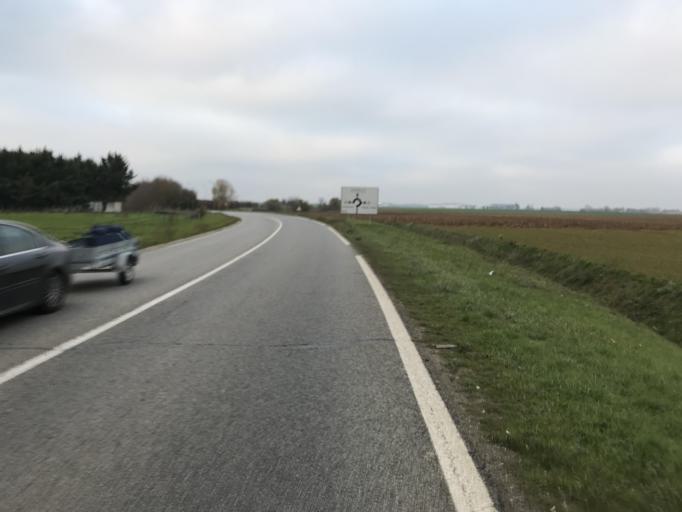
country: FR
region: Ile-de-France
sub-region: Departement des Yvelines
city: Chateaufort
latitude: 48.7377
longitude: 2.0974
